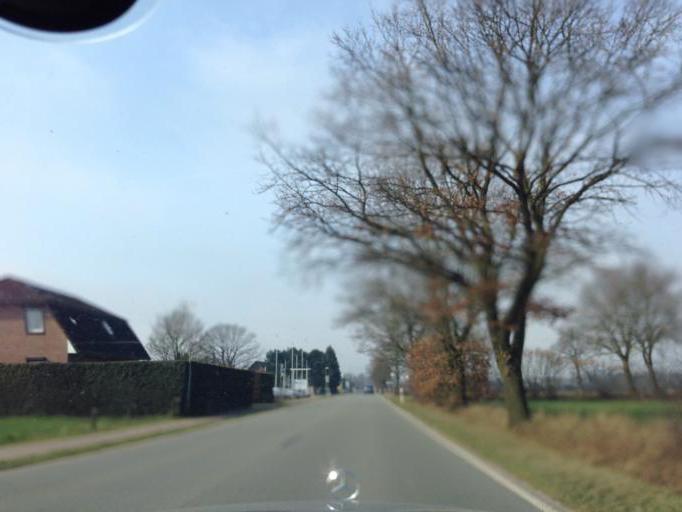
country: DE
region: Schleswig-Holstein
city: Stapelfeld
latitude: 53.6053
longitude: 10.2086
